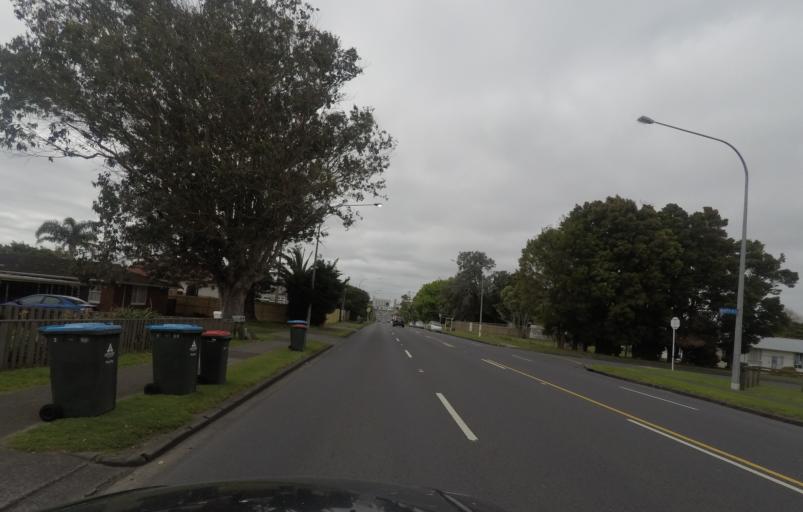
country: NZ
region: Auckland
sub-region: Auckland
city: Wiri
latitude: -36.9531
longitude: 174.8465
